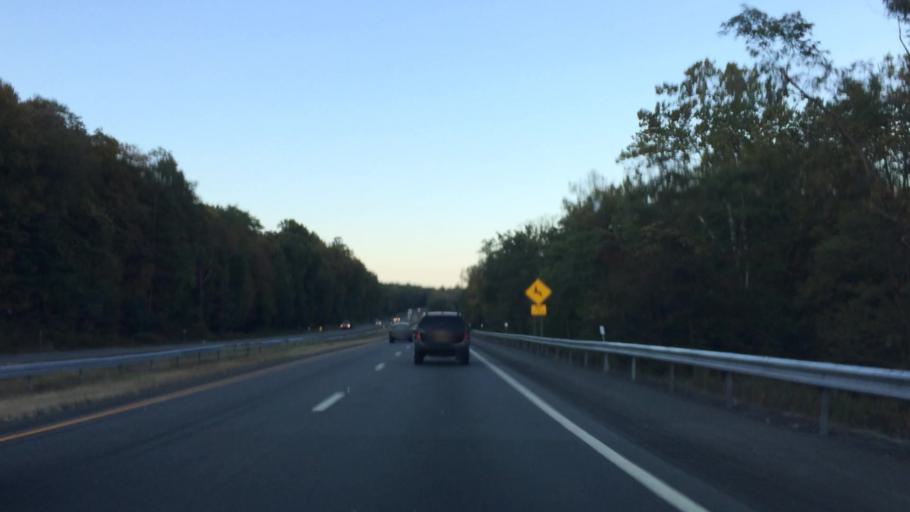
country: US
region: New York
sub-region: Orange County
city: Woodbury
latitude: 41.3887
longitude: -74.0971
